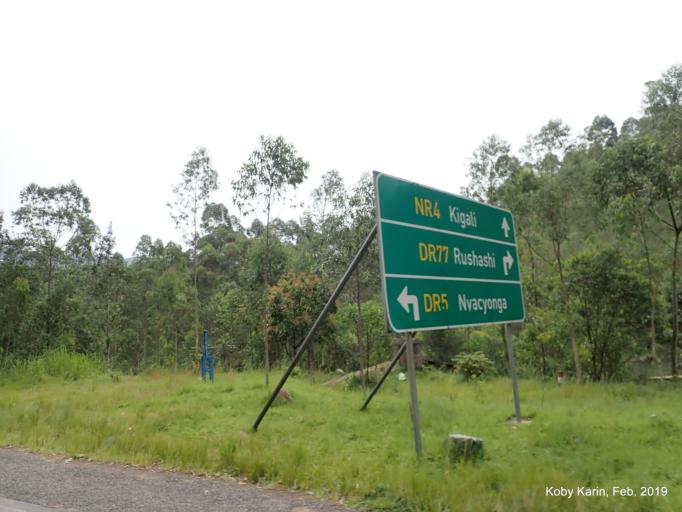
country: RW
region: Northern Province
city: Byumba
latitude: -1.6529
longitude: 29.8527
